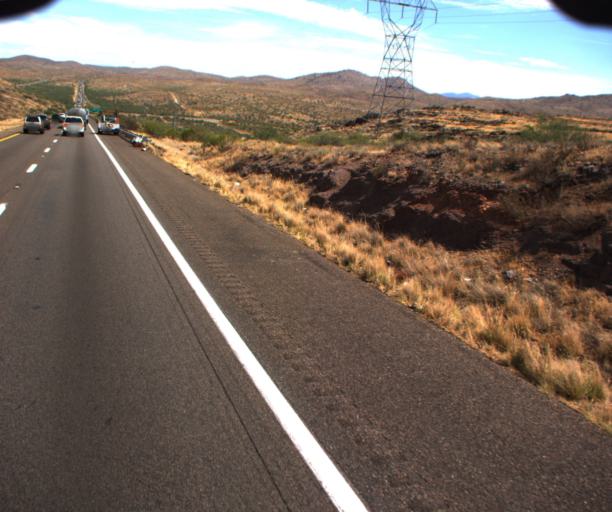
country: US
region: Arizona
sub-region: Yavapai County
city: Cordes Lakes
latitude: 34.2289
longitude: -112.1111
